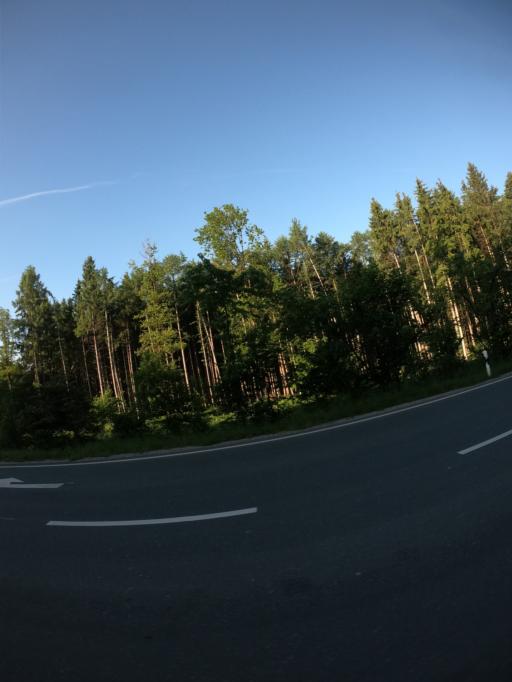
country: DE
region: Bavaria
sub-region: Upper Bavaria
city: Inning am Holz
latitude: 48.3378
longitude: 12.0336
